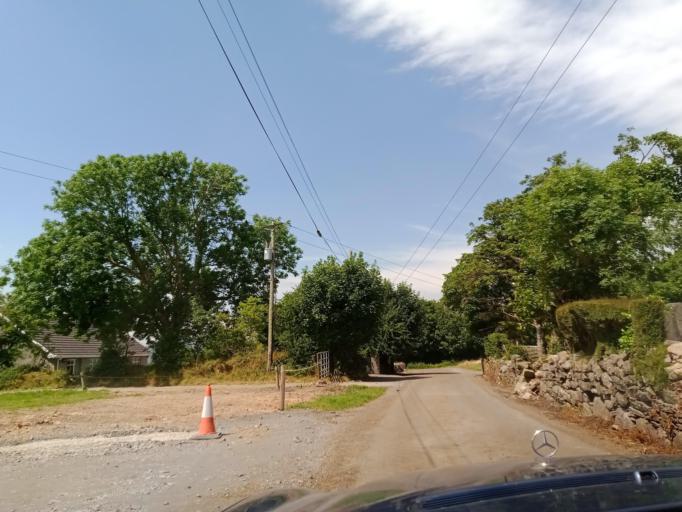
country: IE
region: Leinster
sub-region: Kilkenny
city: Mooncoin
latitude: 52.2667
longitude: -7.2321
